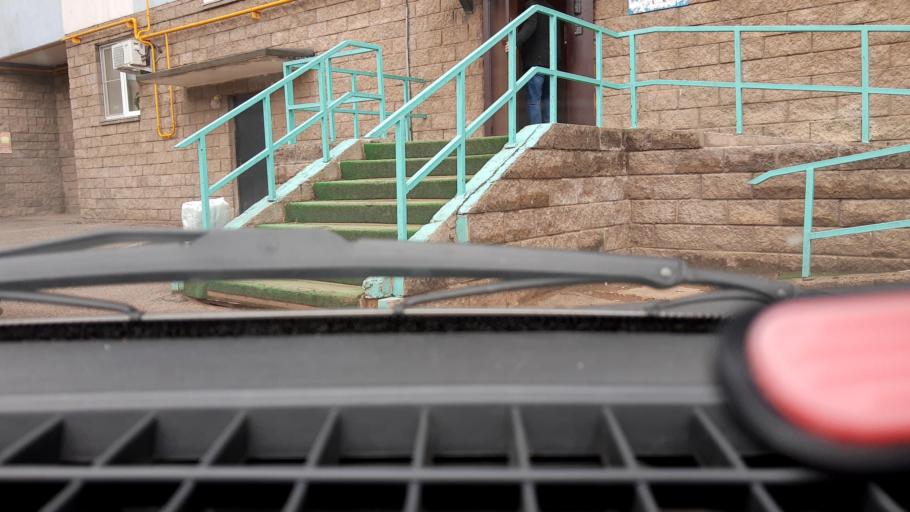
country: RU
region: Bashkortostan
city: Ufa
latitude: 54.7606
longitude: 56.0492
